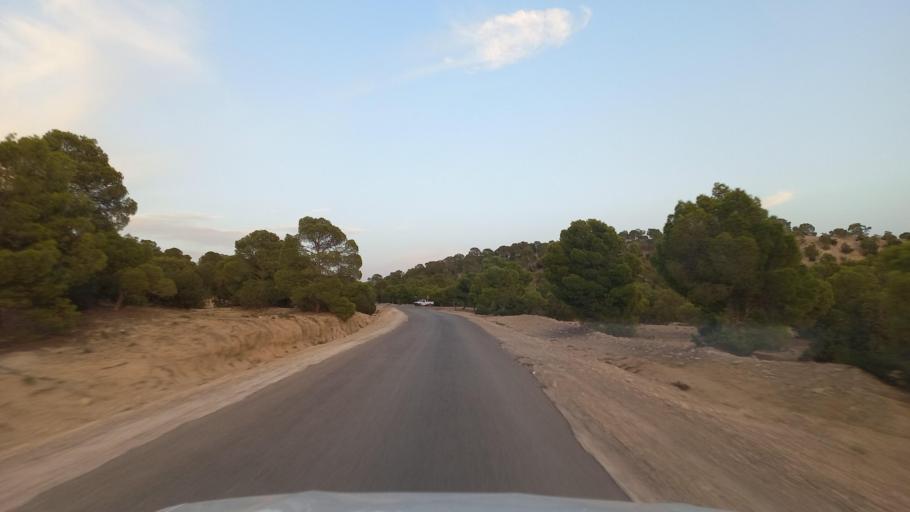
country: TN
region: Al Qasrayn
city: Sbiba
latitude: 35.4108
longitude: 8.9608
